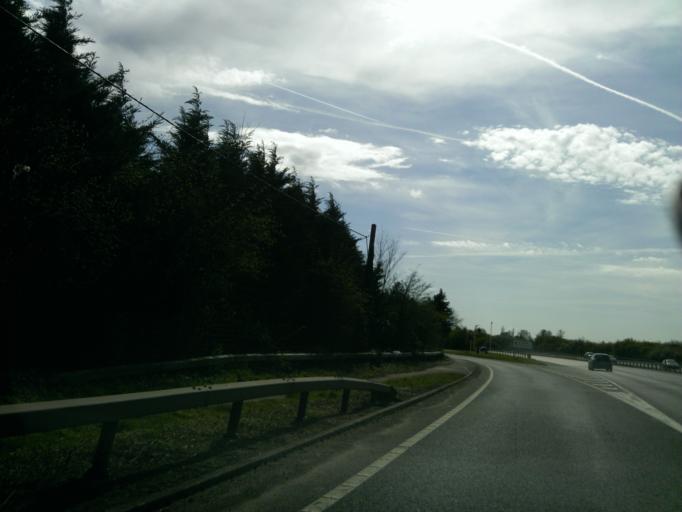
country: GB
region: England
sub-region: Essex
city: Kelvedon
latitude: 51.8504
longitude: 0.7279
